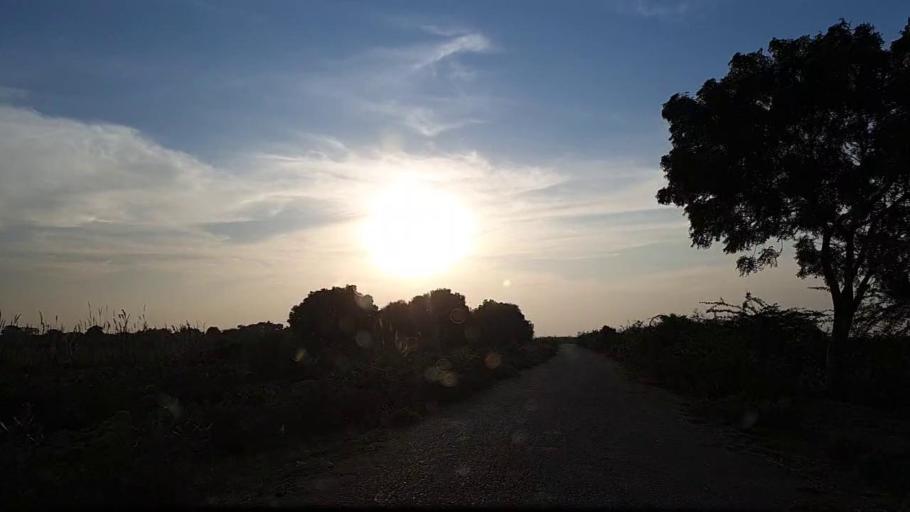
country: PK
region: Sindh
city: Mirpur Batoro
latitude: 24.6400
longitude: 68.1399
